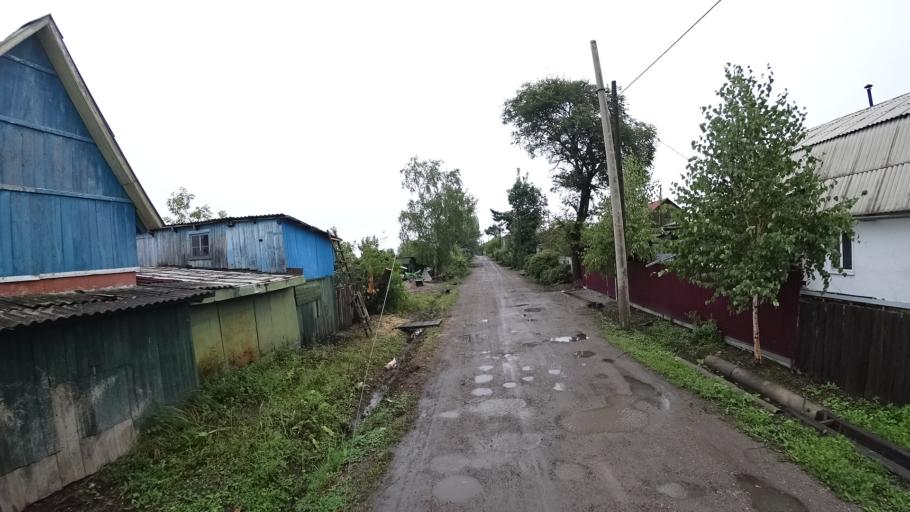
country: RU
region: Primorskiy
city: Monastyrishche
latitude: 44.2036
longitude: 132.4247
